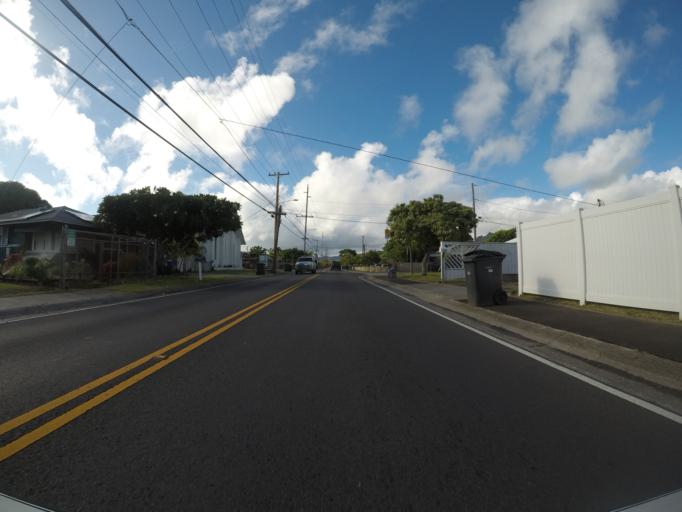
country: US
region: Hawaii
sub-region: Honolulu County
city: Kailua
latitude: 21.4028
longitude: -157.7494
